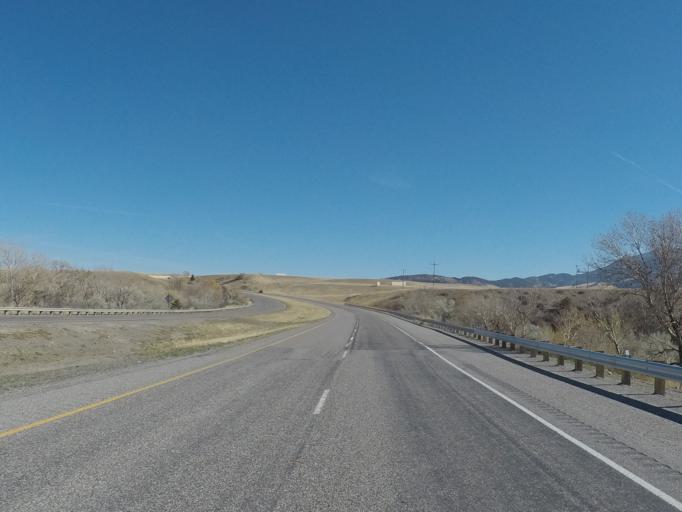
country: US
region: Montana
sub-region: Park County
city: Livingston
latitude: 45.6444
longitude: -110.5586
